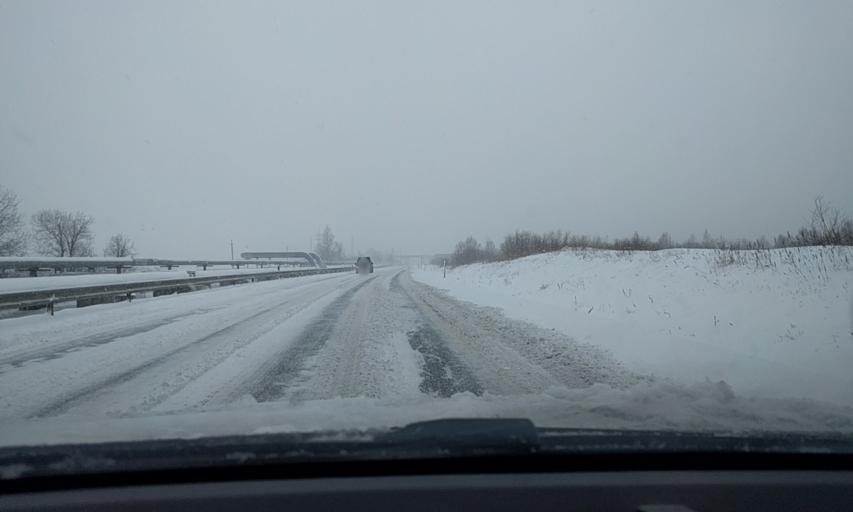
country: EE
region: Harju
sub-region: Maardu linn
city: Maardu
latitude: 59.4730
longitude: 24.9813
